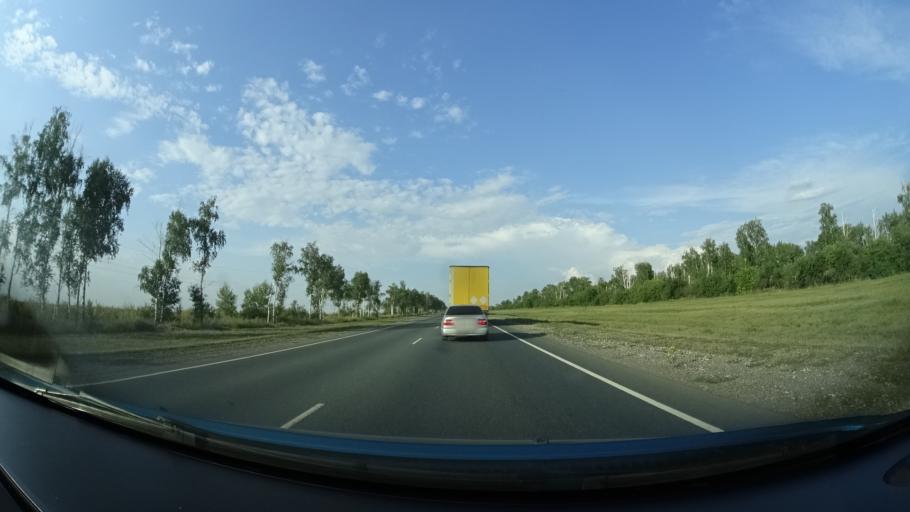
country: RU
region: Samara
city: Krasnyy Yar
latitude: 53.6629
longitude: 50.7569
